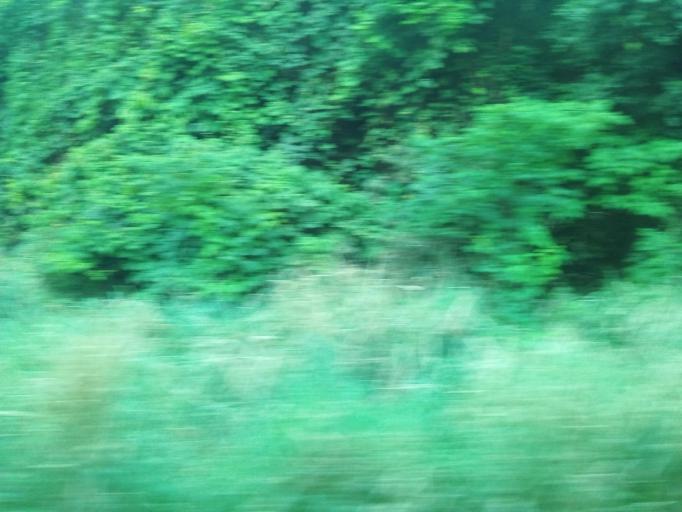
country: BR
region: Minas Gerais
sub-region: Timoteo
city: Timoteo
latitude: -19.5386
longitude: -42.6901
